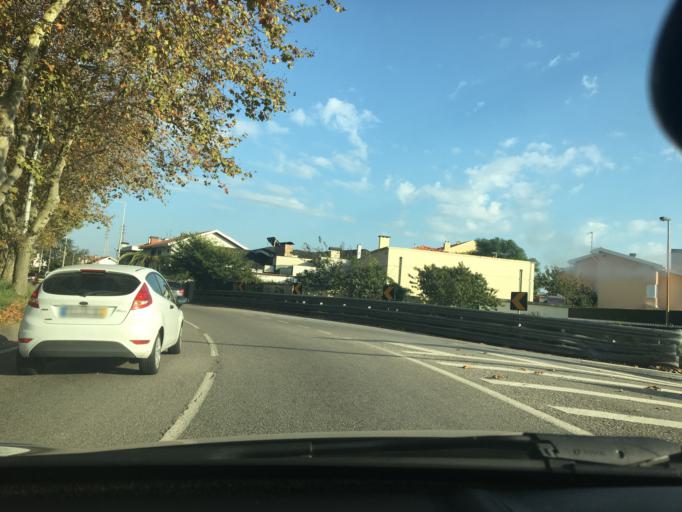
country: PT
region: Porto
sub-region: Matosinhos
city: Senhora da Hora
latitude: 41.1769
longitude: -8.6620
